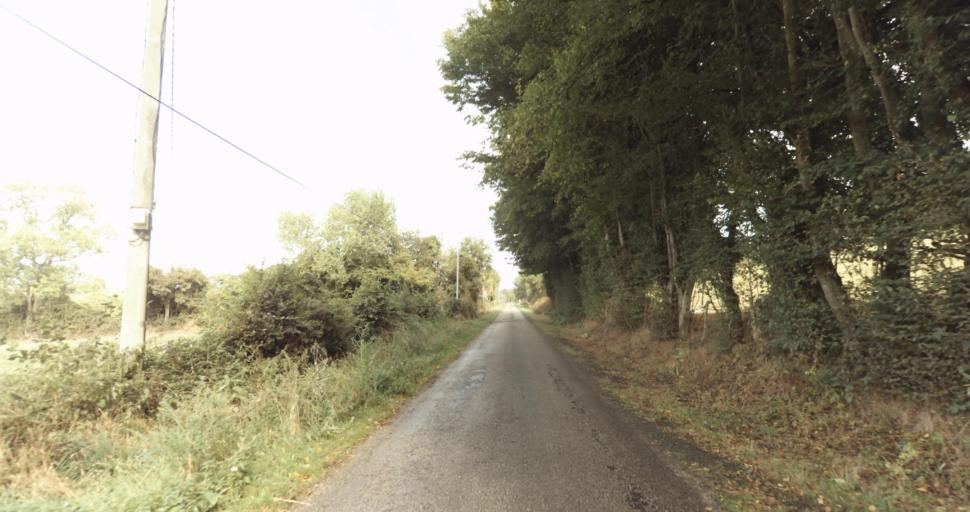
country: FR
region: Lower Normandy
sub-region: Departement de l'Orne
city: Vimoutiers
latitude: 48.8580
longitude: 0.1499
